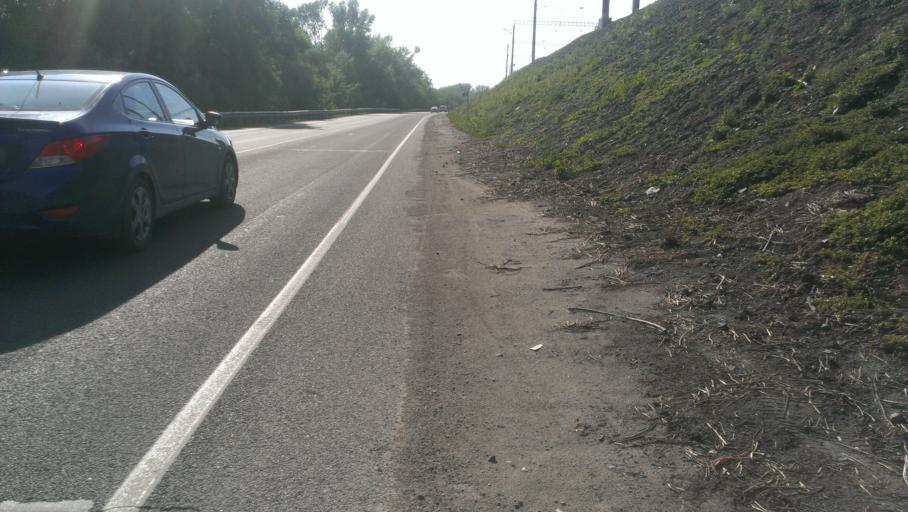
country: RU
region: Altai Krai
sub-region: Gorod Barnaulskiy
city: Barnaul
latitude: 53.3673
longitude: 83.8369
